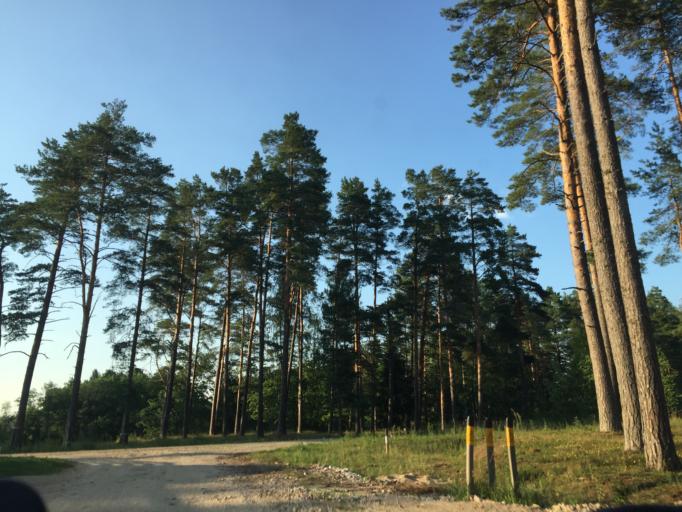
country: LV
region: Riga
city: Bergi
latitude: 56.9779
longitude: 24.3724
